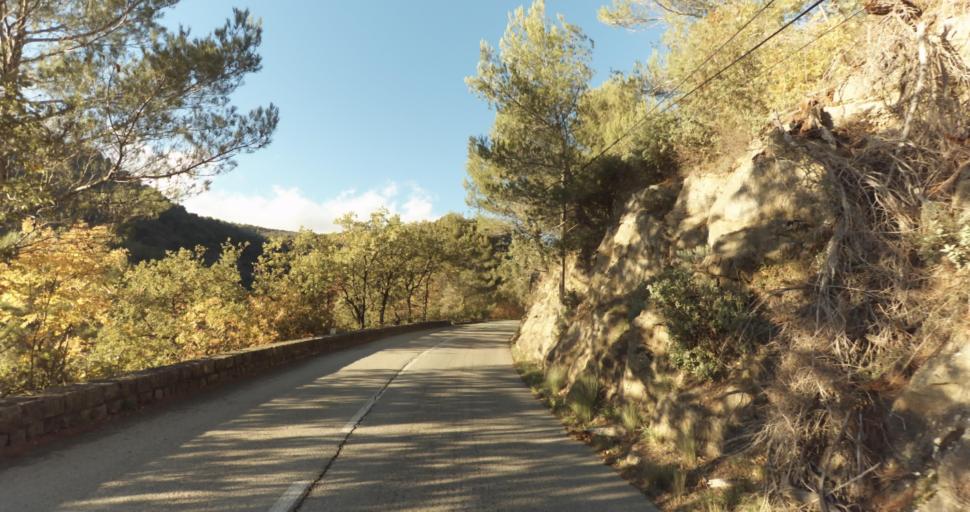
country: FR
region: Provence-Alpes-Cote d'Azur
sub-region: Departement des Alpes-Maritimes
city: Vence
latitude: 43.7346
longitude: 7.1051
